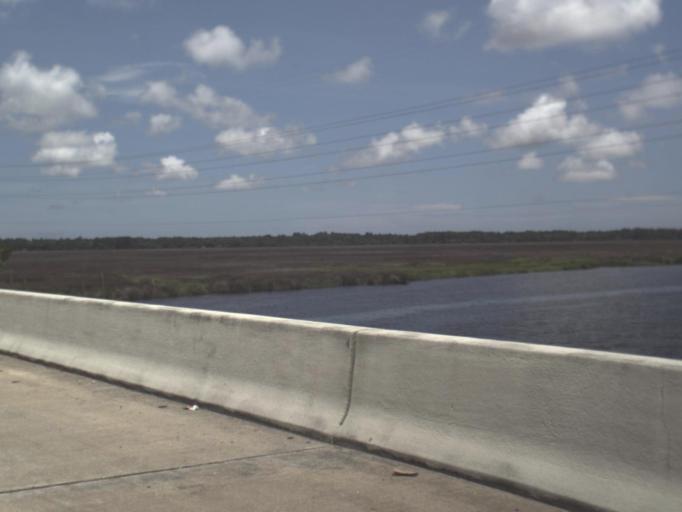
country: US
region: Florida
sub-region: Nassau County
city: Yulee
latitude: 30.5747
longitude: -81.6088
